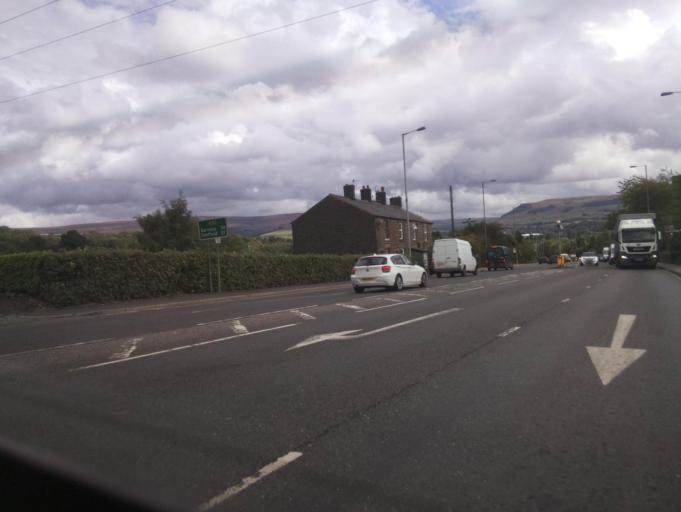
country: GB
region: England
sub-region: Borough of Tameside
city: Longdendale
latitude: 53.4594
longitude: -2.0058
